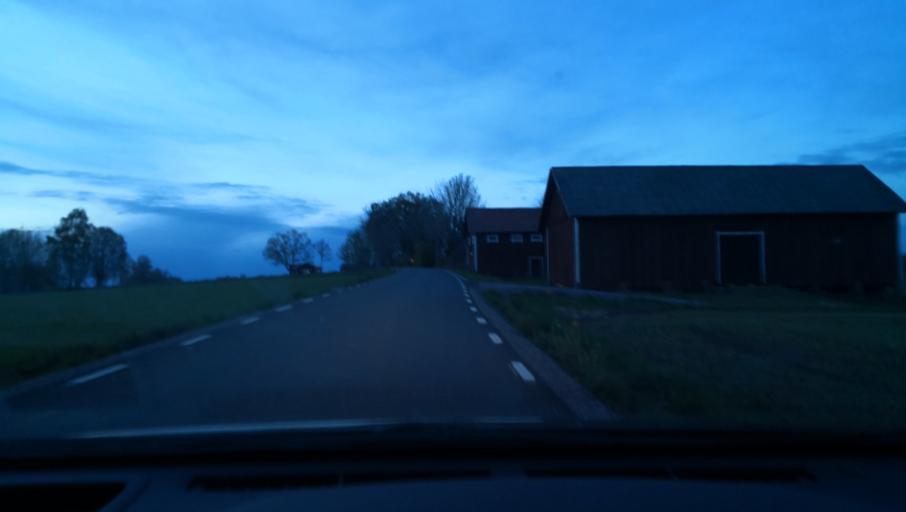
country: SE
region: OErebro
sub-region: Askersunds Kommun
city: Asbro
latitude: 59.0482
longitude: 14.9290
